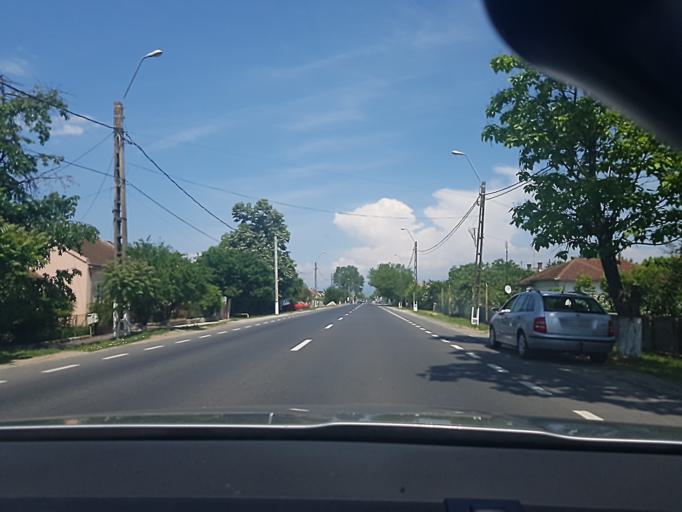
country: RO
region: Hunedoara
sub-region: Comuna Calan
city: Calan
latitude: 45.7318
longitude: 22.9967
